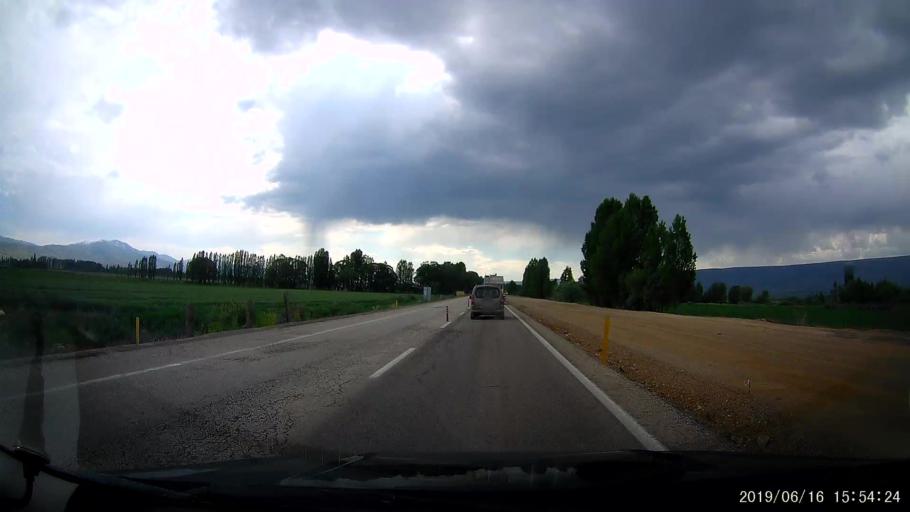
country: TR
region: Erzurum
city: Pasinler
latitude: 39.9776
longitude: 41.6344
